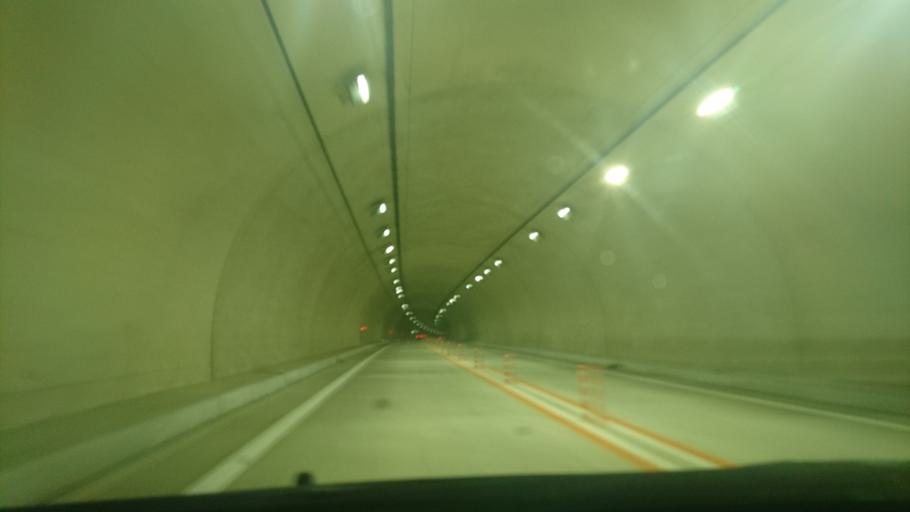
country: JP
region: Iwate
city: Kamaishi
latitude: 39.2846
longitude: 141.8618
